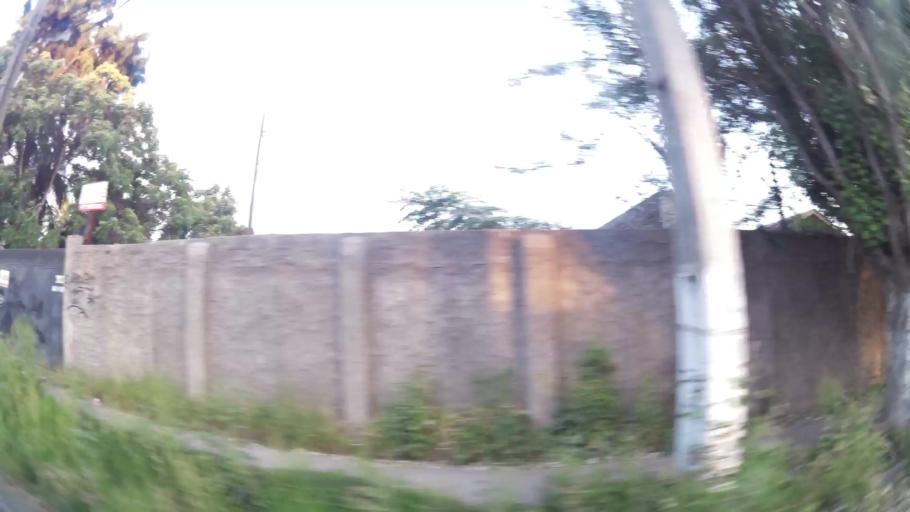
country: CL
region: Santiago Metropolitan
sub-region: Provincia de Maipo
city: San Bernardo
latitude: -33.6180
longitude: -70.6982
